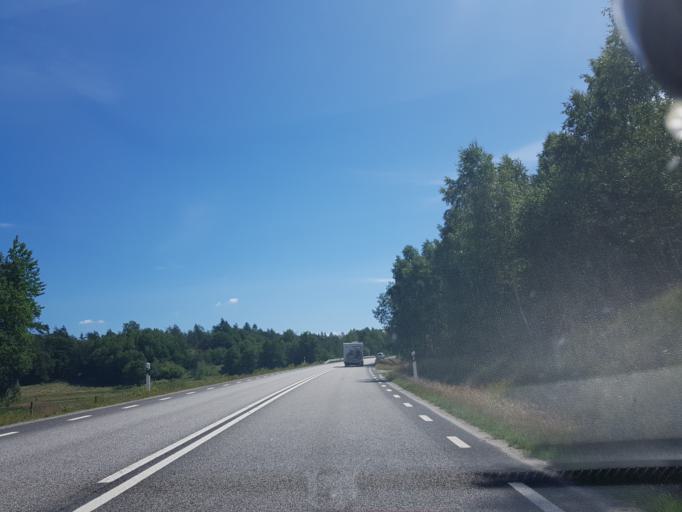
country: SE
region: Vaestra Goetaland
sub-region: Orust
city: Henan
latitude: 58.1467
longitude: 11.6255
